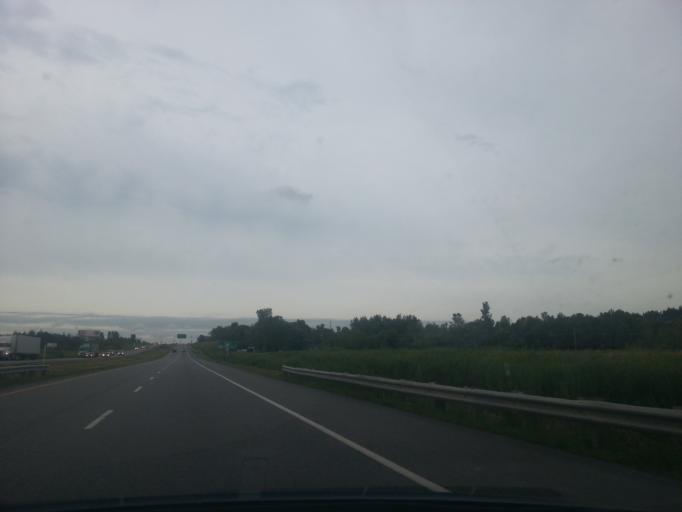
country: CA
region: Quebec
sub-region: Monteregie
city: Vaudreuil-Dorion
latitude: 45.3854
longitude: -74.0572
